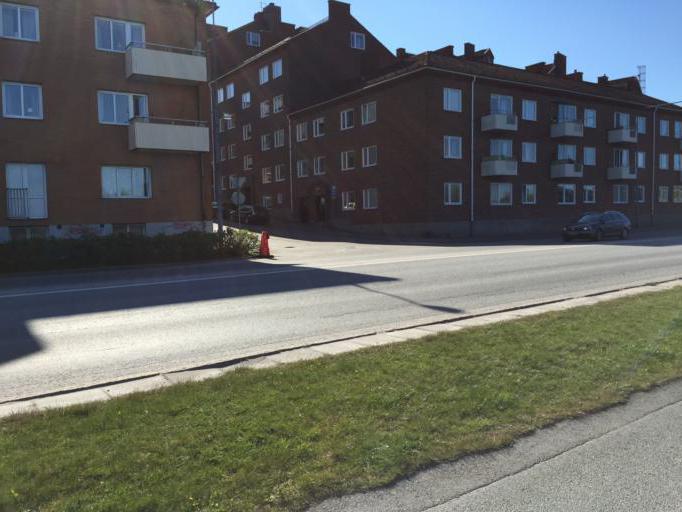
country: SE
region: Blekinge
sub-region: Karlskrona Kommun
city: Karlskrona
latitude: 56.1648
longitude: 15.5807
